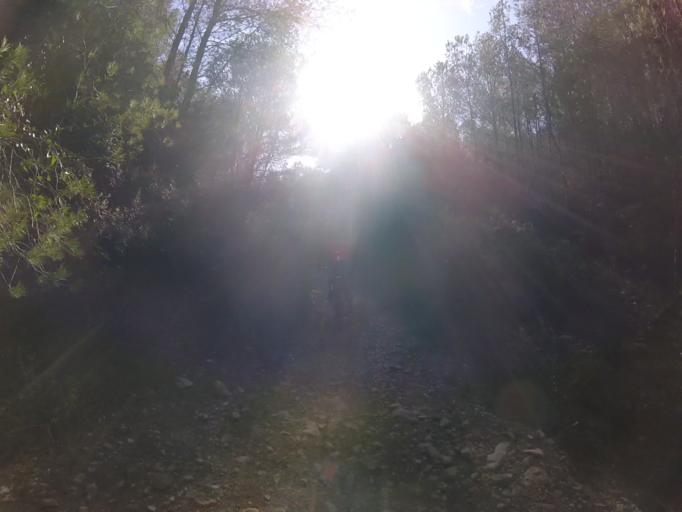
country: ES
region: Valencia
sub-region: Provincia de Castello
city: Santa Magdalena de Pulpis
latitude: 40.3103
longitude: 0.3335
